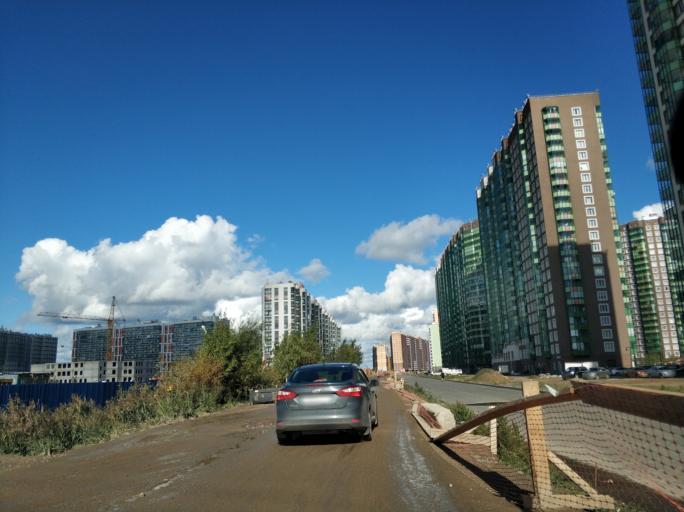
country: RU
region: St.-Petersburg
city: Grazhdanka
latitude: 60.0552
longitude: 30.4206
